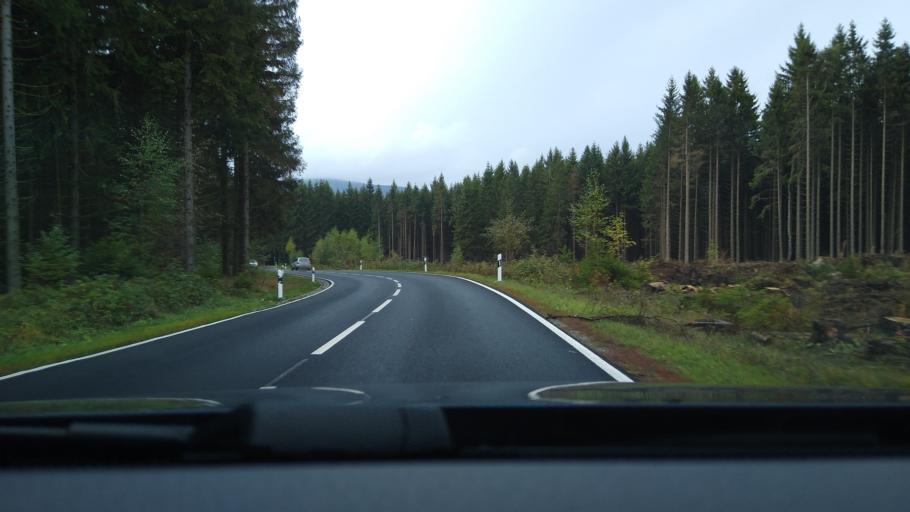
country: DE
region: Saxony-Anhalt
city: Elbingerode
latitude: 51.7721
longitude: 10.7481
